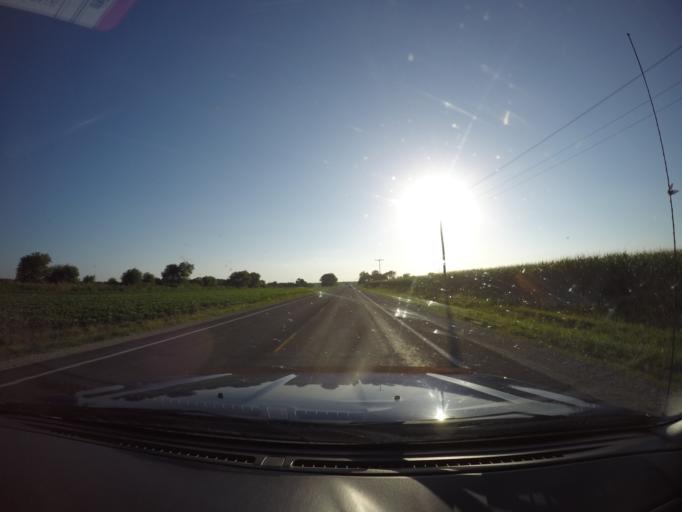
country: US
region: Kansas
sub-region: Pottawatomie County
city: Wamego
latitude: 39.2170
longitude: -96.2084
